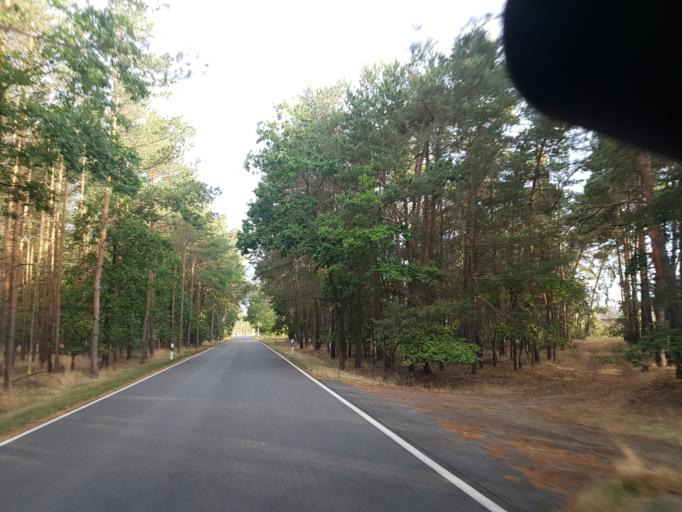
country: DE
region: Saxony-Anhalt
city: Holzdorf
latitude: 51.7991
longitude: 13.0930
